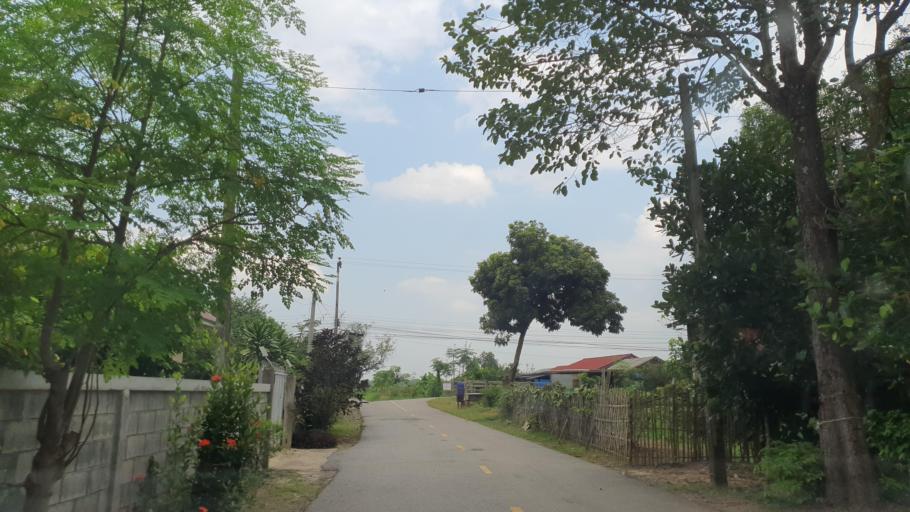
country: TH
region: Sukhothai
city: Thung Saliam
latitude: 17.3193
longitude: 99.5111
